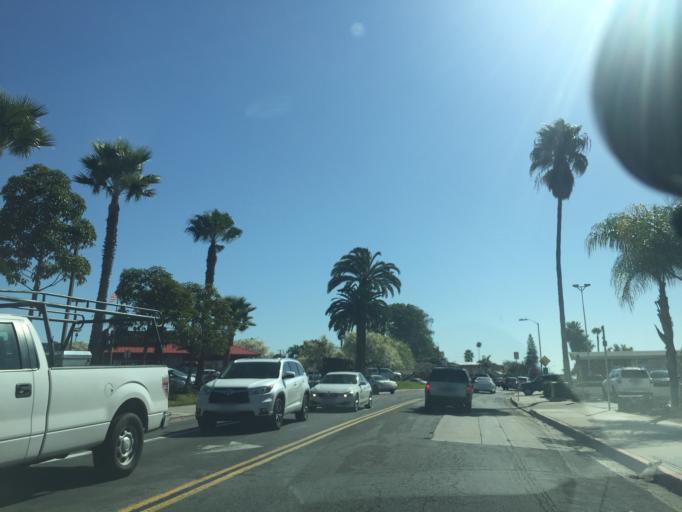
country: US
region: California
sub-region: San Diego County
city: San Diego
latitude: 32.7943
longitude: -117.1941
